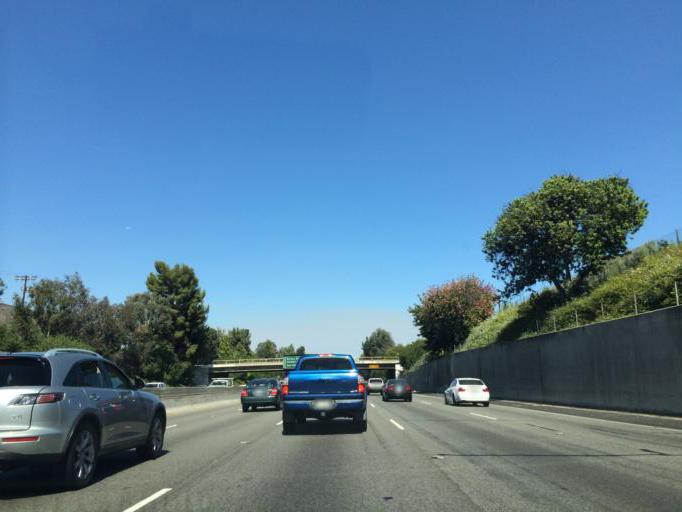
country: US
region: California
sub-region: Los Angeles County
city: Northridge
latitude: 34.1711
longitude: -118.5115
